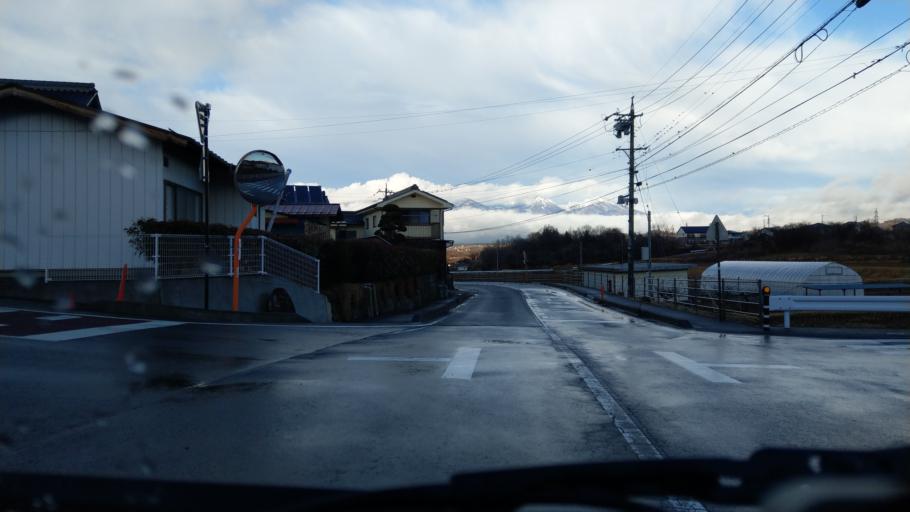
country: JP
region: Nagano
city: Kamimaruko
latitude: 36.2835
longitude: 138.3288
